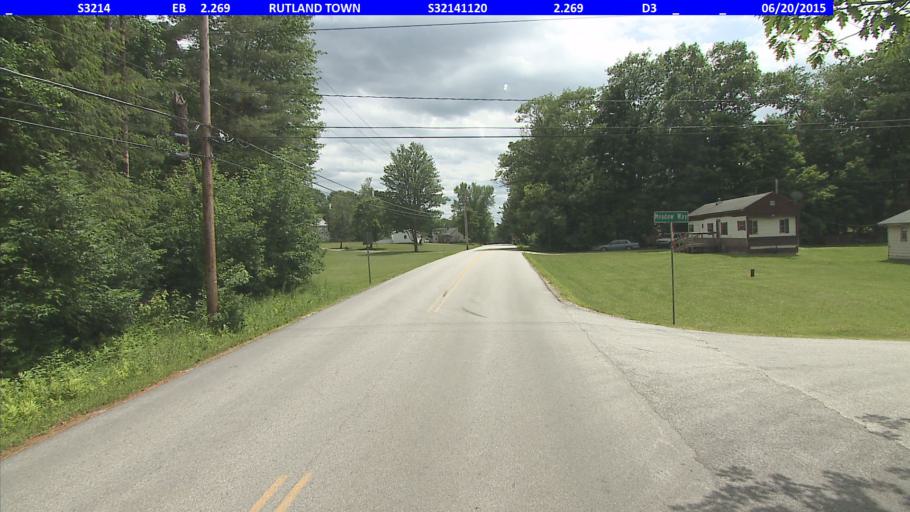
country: US
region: Vermont
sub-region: Rutland County
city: Rutland
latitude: 43.6334
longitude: -72.9436
